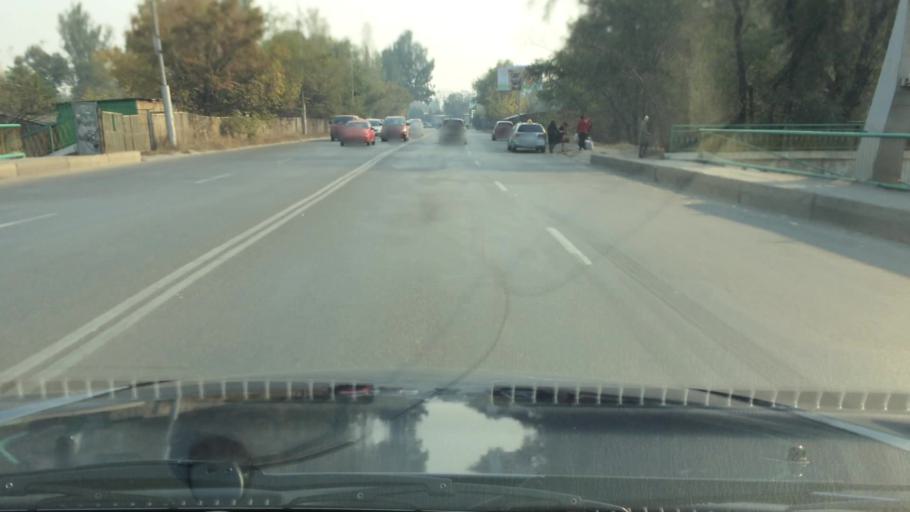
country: KG
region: Chuy
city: Bishkek
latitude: 42.8627
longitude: 74.6108
